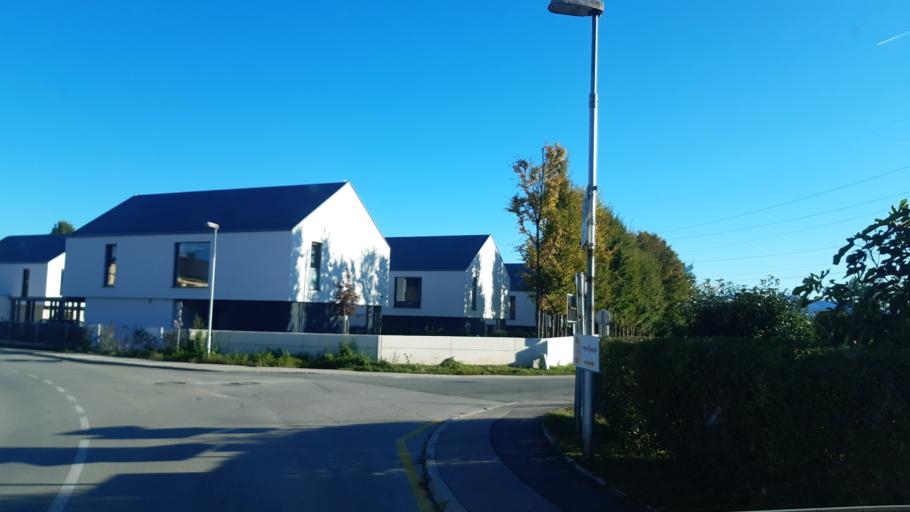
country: SI
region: Kranj
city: Zgornje Bitnje
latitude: 46.2293
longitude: 14.3373
